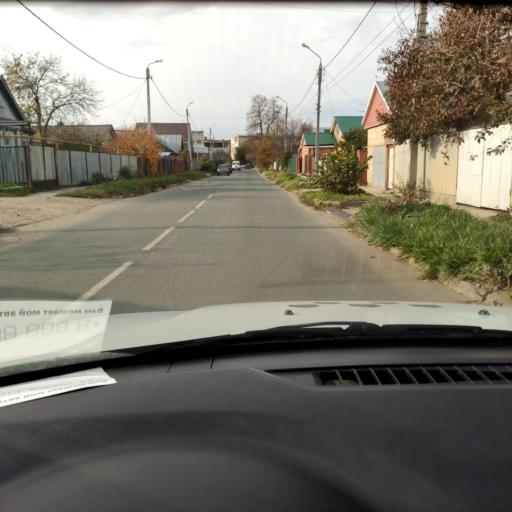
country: RU
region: Samara
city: Tol'yatti
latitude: 53.5249
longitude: 49.4181
